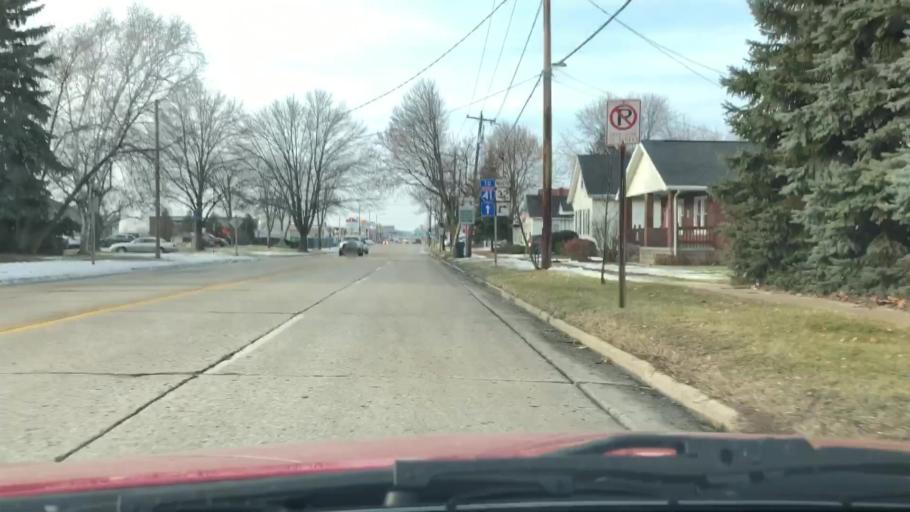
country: US
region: Wisconsin
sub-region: Brown County
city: De Pere
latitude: 44.4489
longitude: -88.0788
